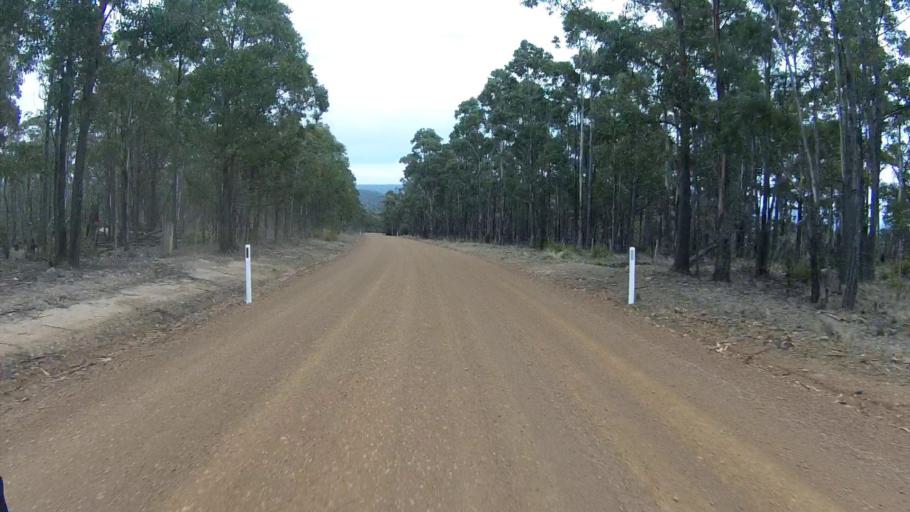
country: AU
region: Tasmania
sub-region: Sorell
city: Sorell
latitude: -42.5855
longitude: 147.8840
